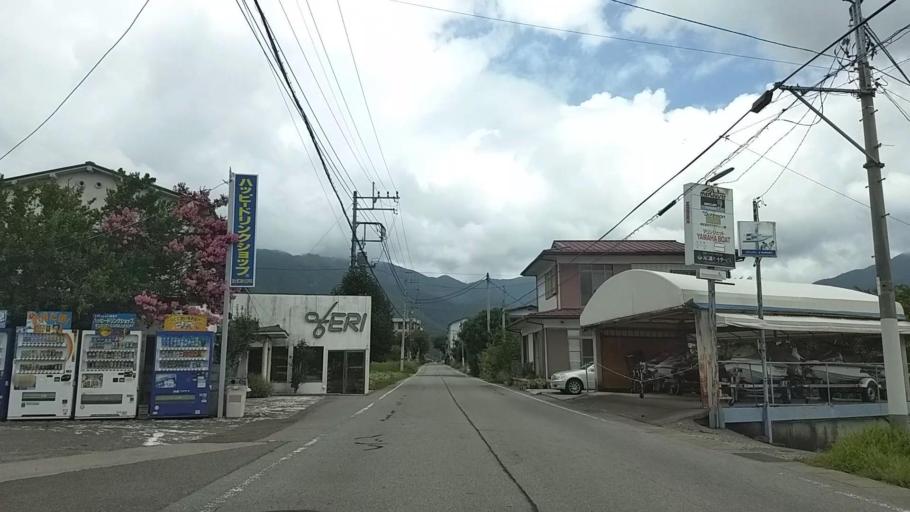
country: JP
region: Yamanashi
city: Fujikawaguchiko
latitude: 35.5067
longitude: 138.7589
